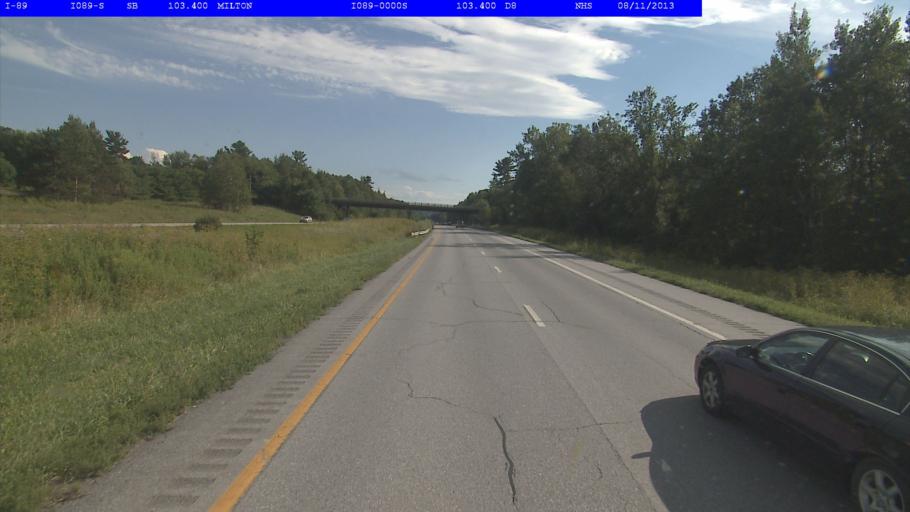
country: US
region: Vermont
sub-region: Chittenden County
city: Milton
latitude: 44.6623
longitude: -73.1377
